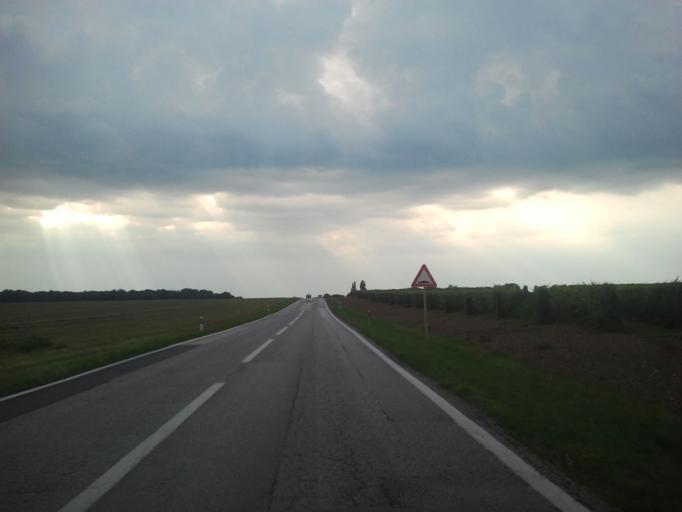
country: HR
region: Vukovarsko-Srijemska
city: Vukovar
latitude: 45.3249
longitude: 19.0601
